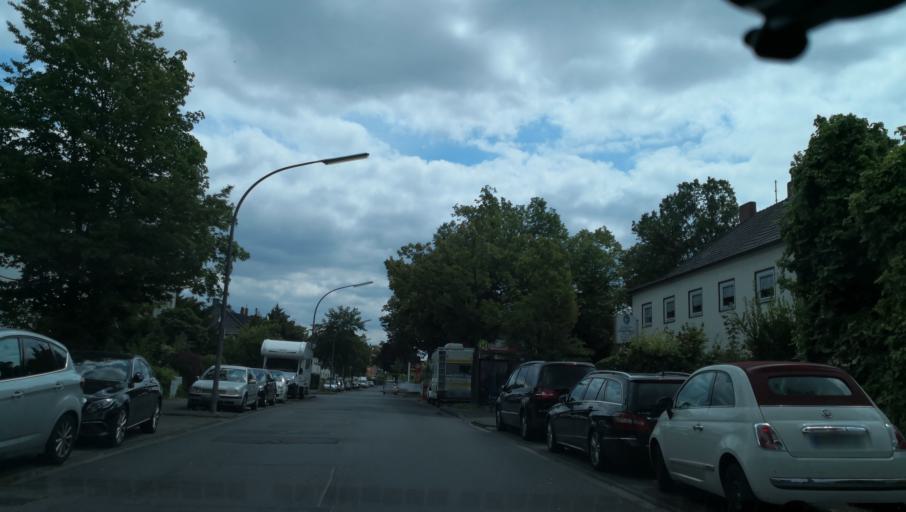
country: DE
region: North Rhine-Westphalia
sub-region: Regierungsbezirk Koln
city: Bilderstoeckchen
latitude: 50.9749
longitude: 6.9392
